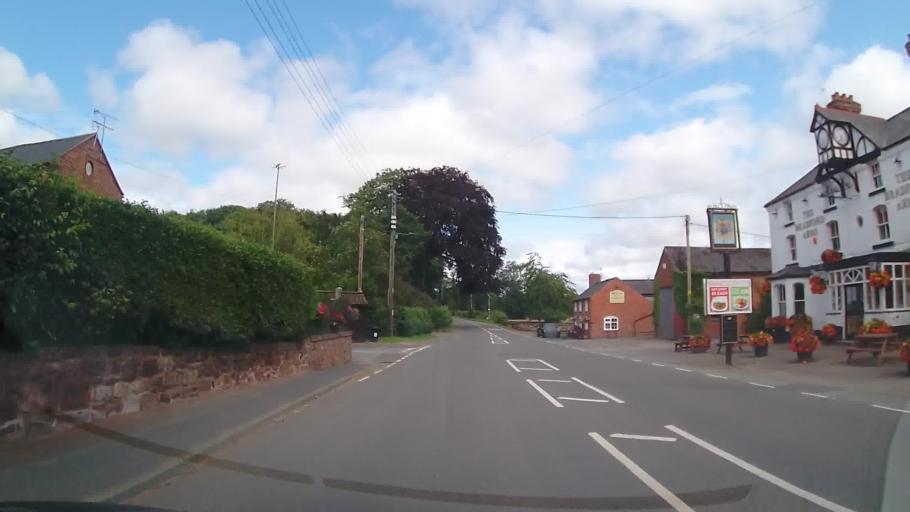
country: GB
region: England
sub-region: Shropshire
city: Whittington
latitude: 52.7941
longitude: -2.9904
